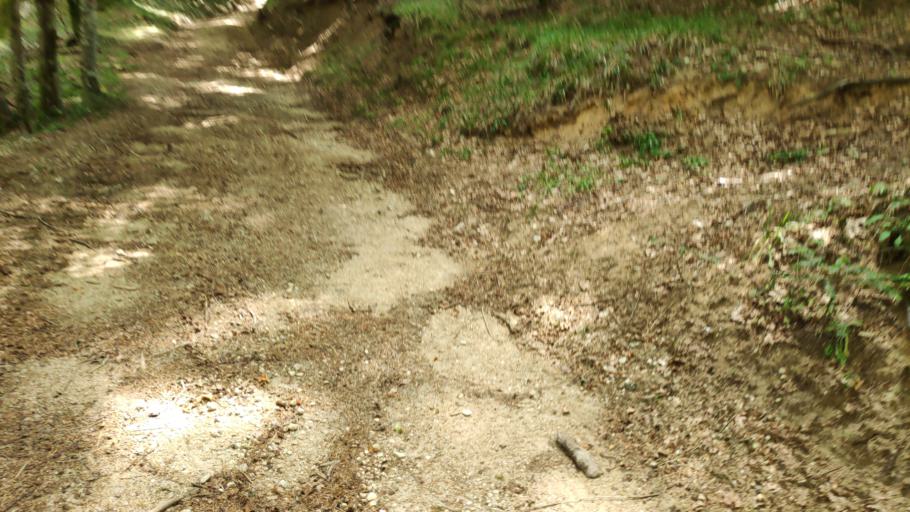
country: IT
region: Calabria
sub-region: Provincia di Vibo-Valentia
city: Serra San Bruno
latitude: 38.5417
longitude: 16.3607
